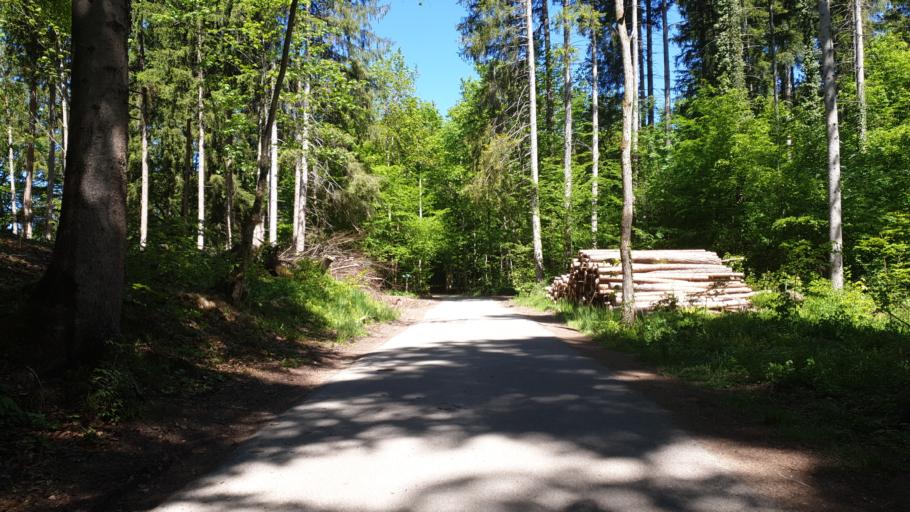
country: DE
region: Bavaria
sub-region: Upper Bavaria
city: Iffeldorf
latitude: 47.7788
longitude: 11.3003
